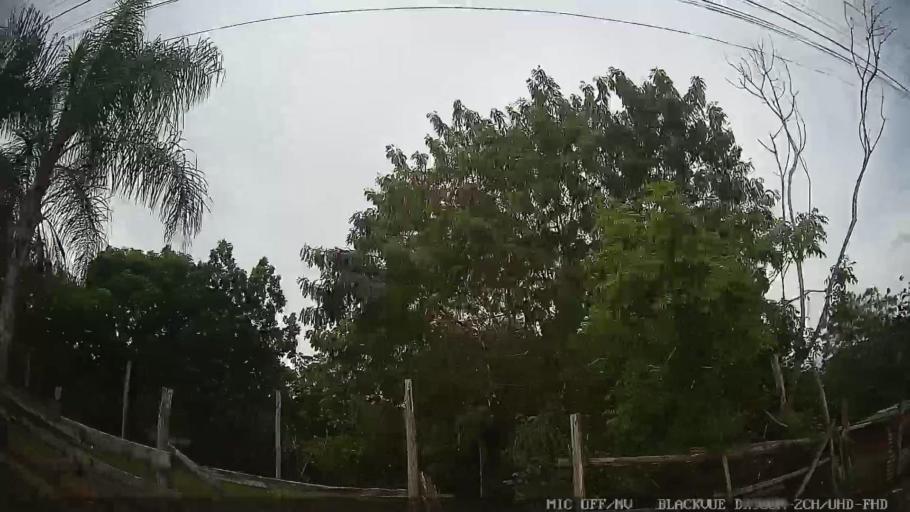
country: BR
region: Sao Paulo
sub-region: Salto
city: Salto
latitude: -23.1960
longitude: -47.2718
